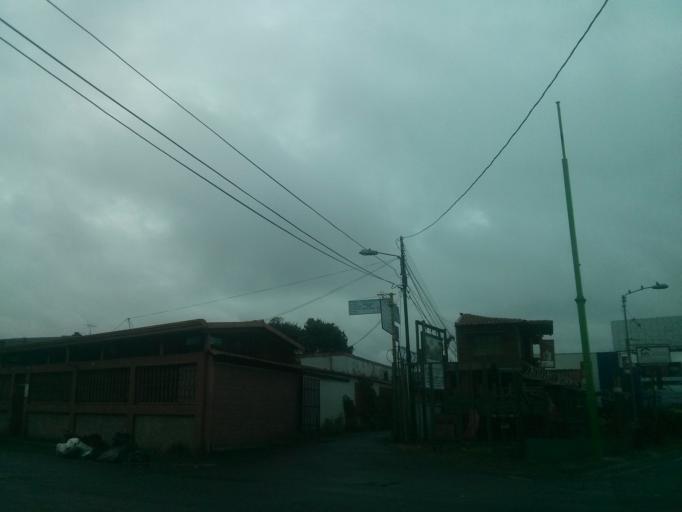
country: CR
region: San Jose
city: San Pedro
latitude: 9.9248
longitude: -84.0564
